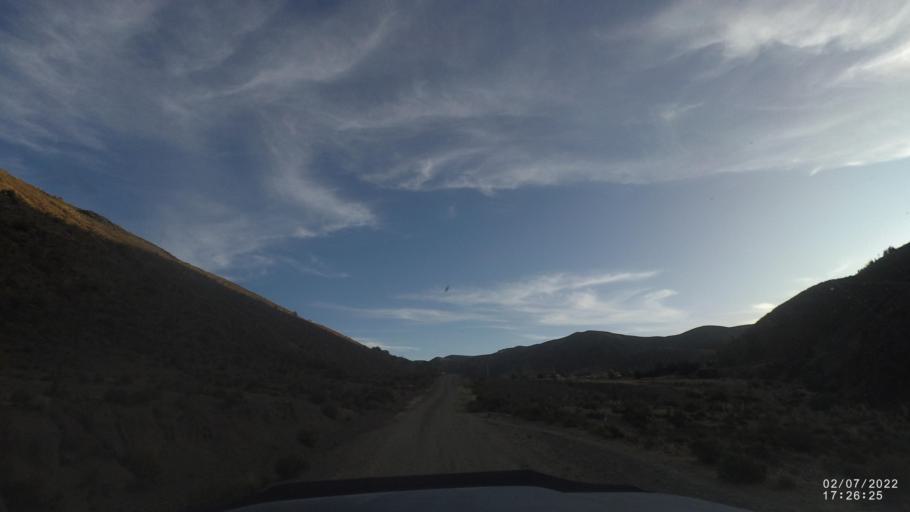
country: BO
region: Cochabamba
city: Irpa Irpa
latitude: -17.8802
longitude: -66.6110
